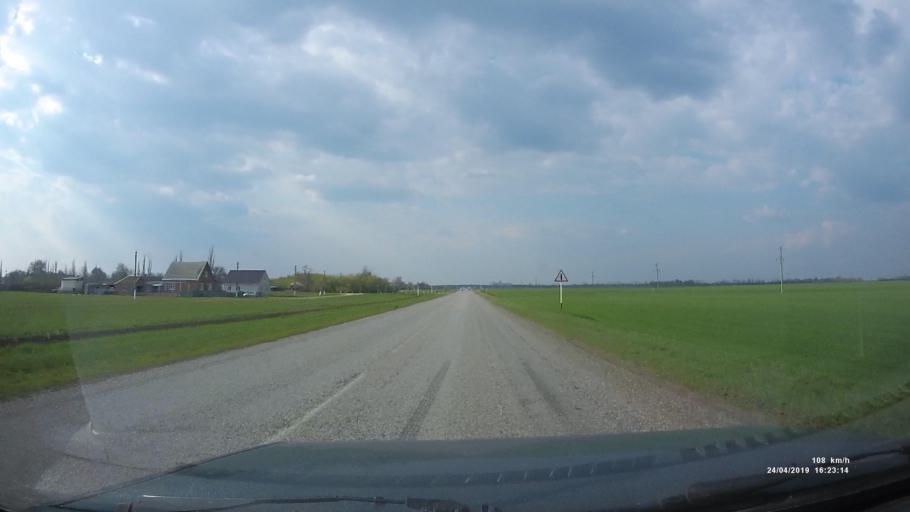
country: RU
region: Rostov
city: Orlovskiy
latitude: 46.8316
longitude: 42.0508
